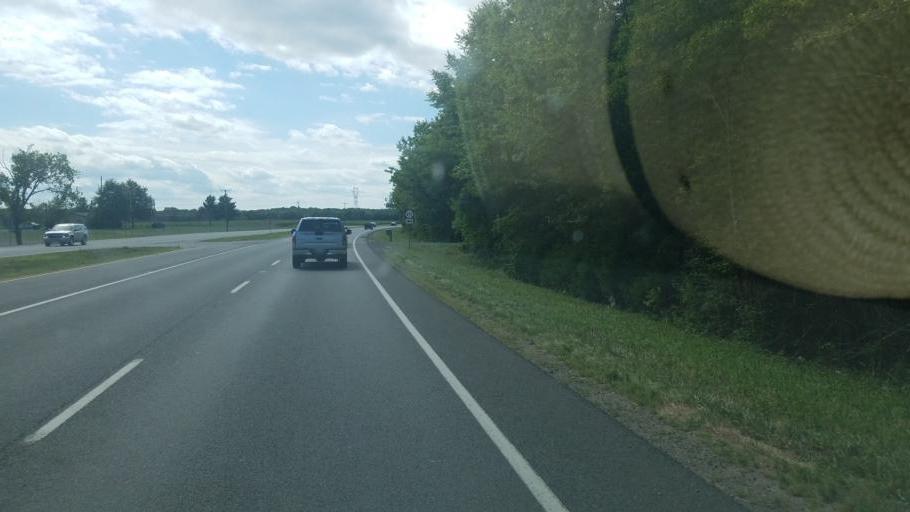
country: US
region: Virginia
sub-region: Fauquier County
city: Bealeton
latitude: 38.5578
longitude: -77.7363
